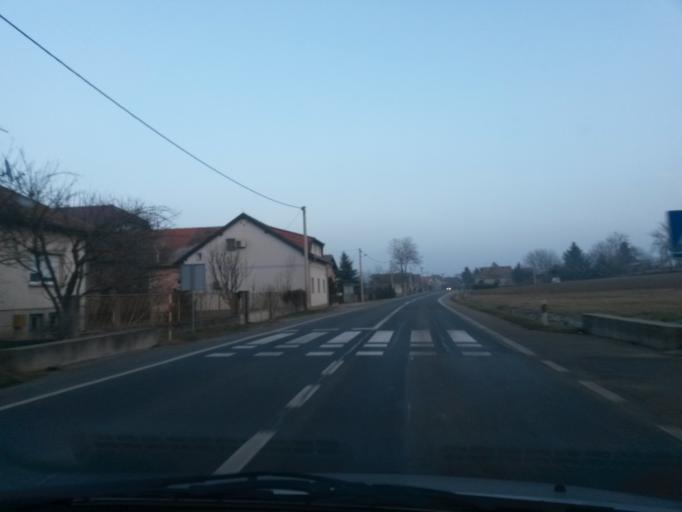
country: HR
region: Varazdinska
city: Ludbreg
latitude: 46.2313
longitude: 16.6599
